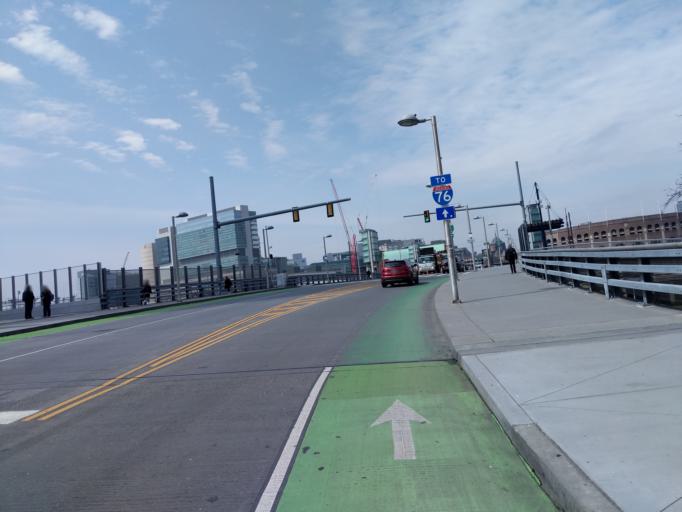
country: US
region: Pennsylvania
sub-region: Philadelphia County
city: Philadelphia
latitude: 39.9463
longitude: -75.1857
